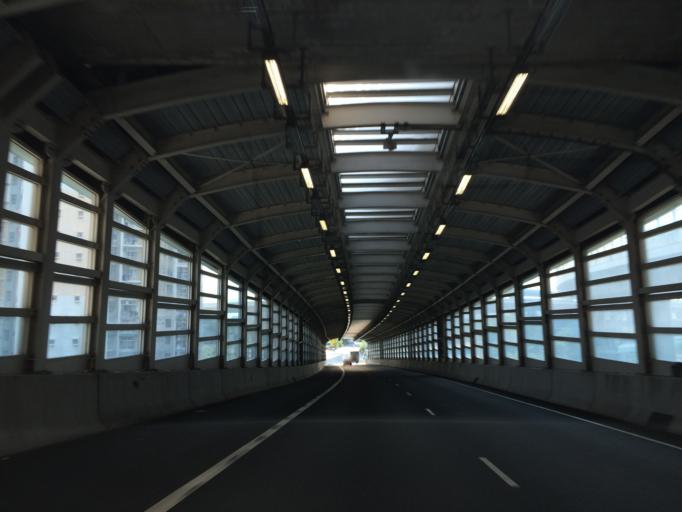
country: HK
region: Sham Shui Po
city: Sham Shui Po
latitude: 22.3339
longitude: 114.1450
